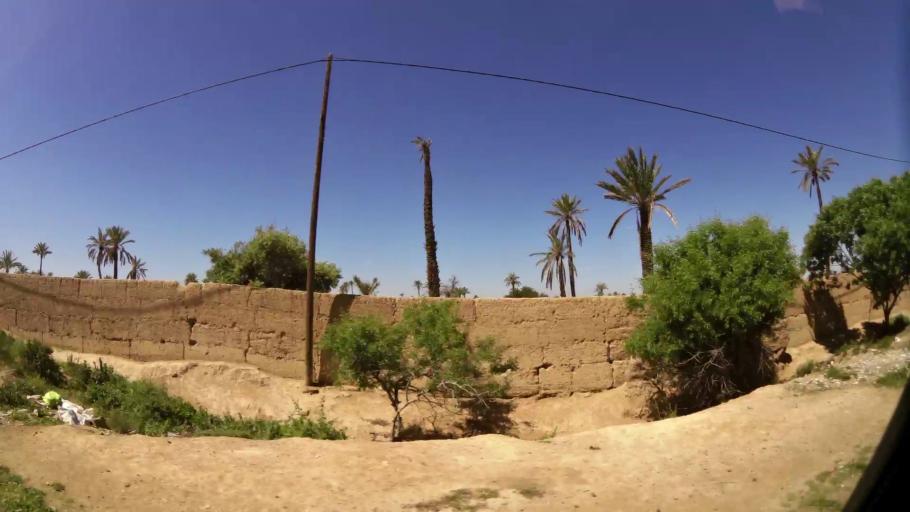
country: MA
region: Marrakech-Tensift-Al Haouz
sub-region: Marrakech
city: Marrakesh
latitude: 31.6709
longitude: -7.9794
